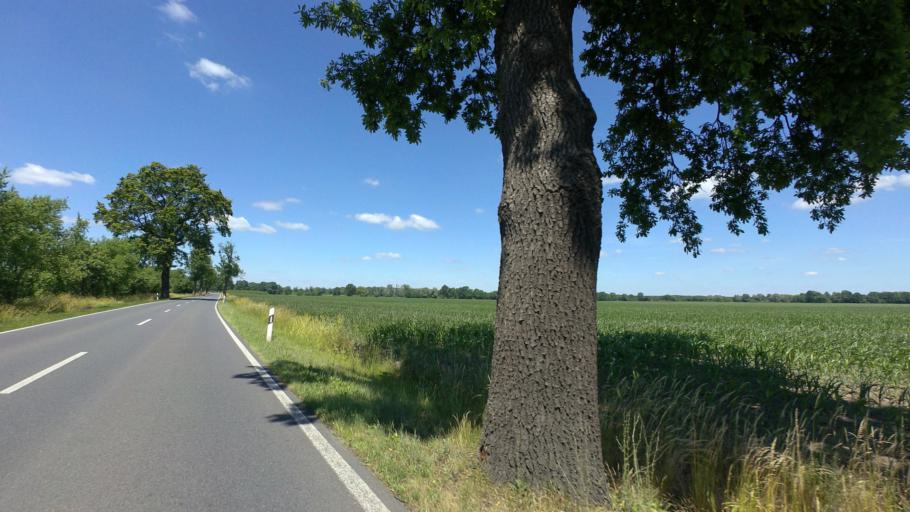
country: DE
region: Brandenburg
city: Golssen
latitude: 51.9571
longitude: 13.6310
